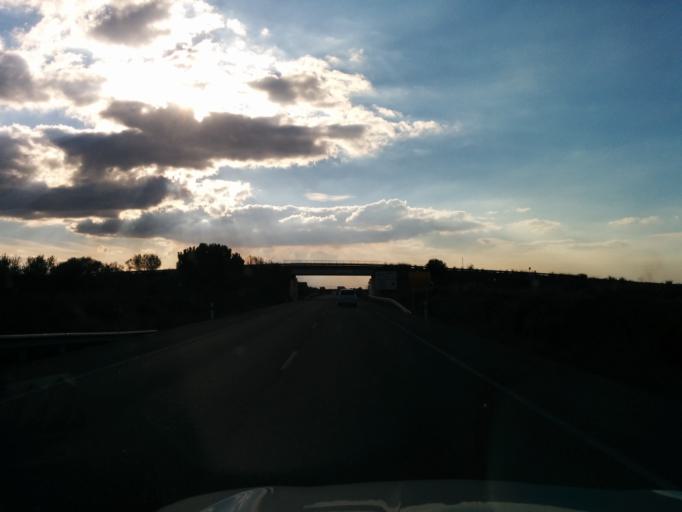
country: ES
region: Andalusia
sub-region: Provincia de Sevilla
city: Utrera
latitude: 37.1610
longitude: -5.7693
